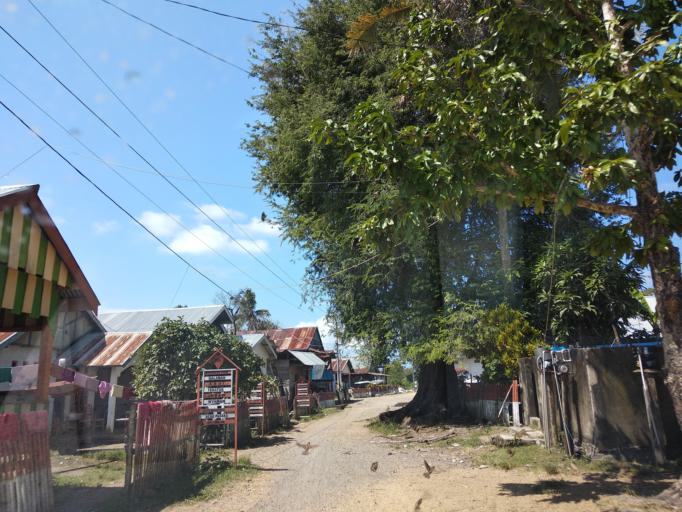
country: ID
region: South Sulawesi
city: Kadai
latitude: -4.7402
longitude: 120.3863
